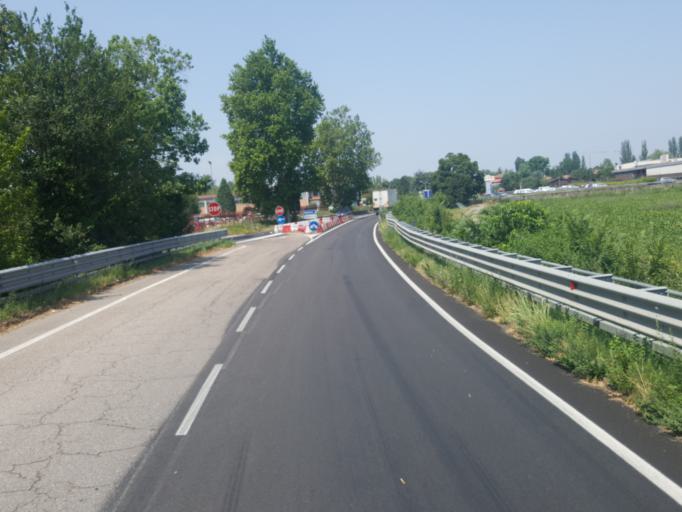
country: IT
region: Emilia-Romagna
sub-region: Provincia di Bologna
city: Anzola dell'Emilia
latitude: 44.5519
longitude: 11.1770
